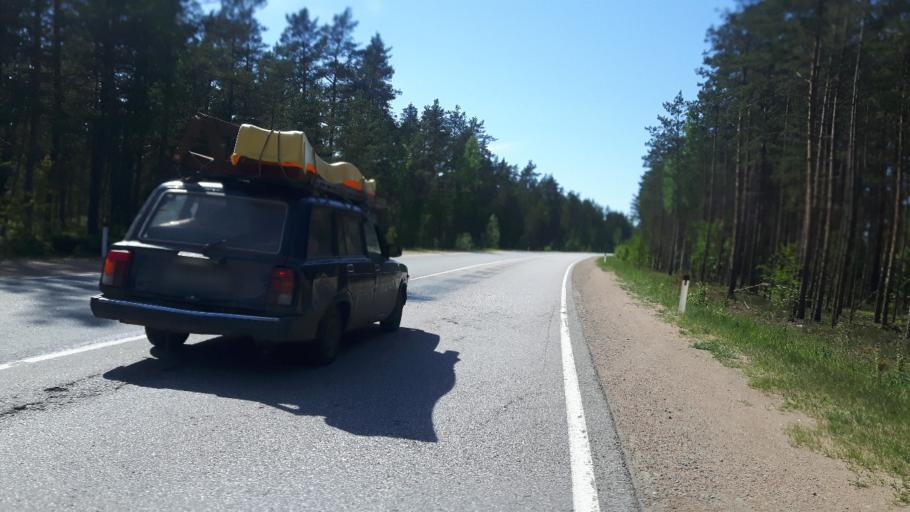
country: RU
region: Leningrad
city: Sista-Palkino
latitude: 59.7679
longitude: 28.8013
